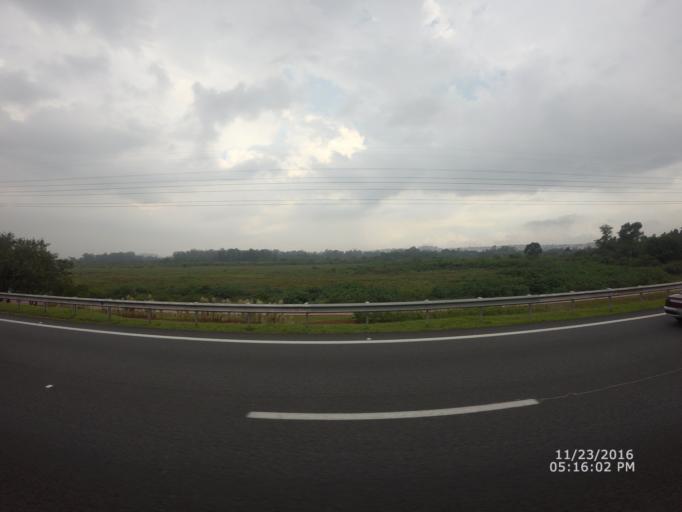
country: BR
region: Sao Paulo
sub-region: Guarulhos
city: Guarulhos
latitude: -23.4855
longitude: -46.5292
